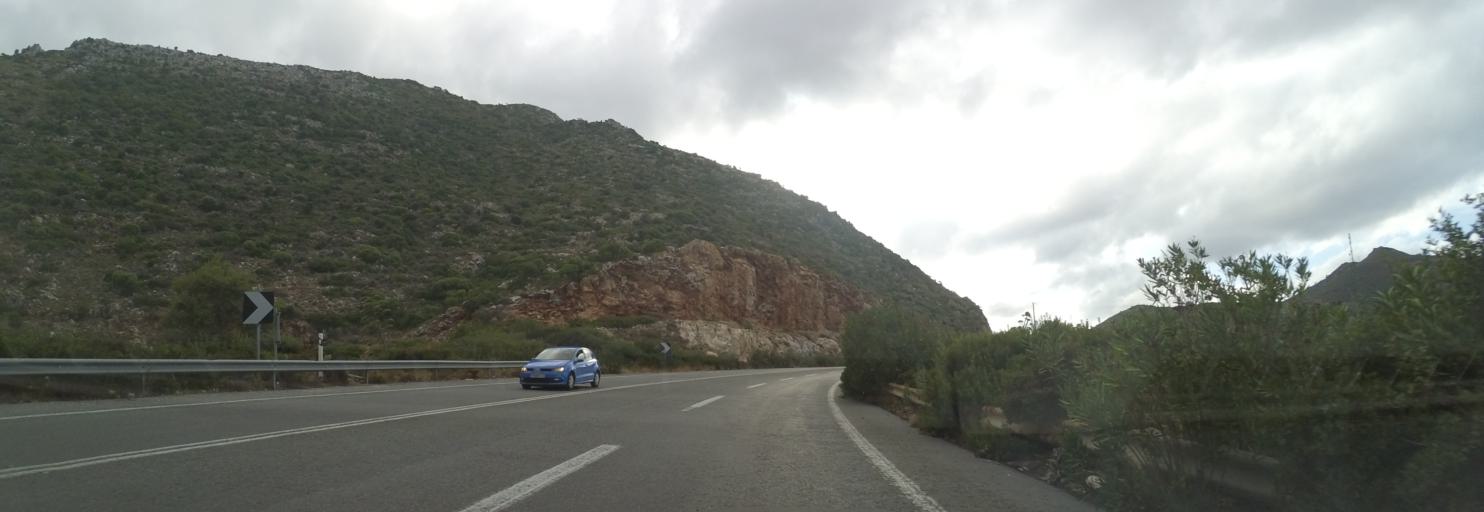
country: GR
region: Crete
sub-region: Nomos Rethymnis
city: Perama
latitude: 35.4081
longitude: 24.7671
